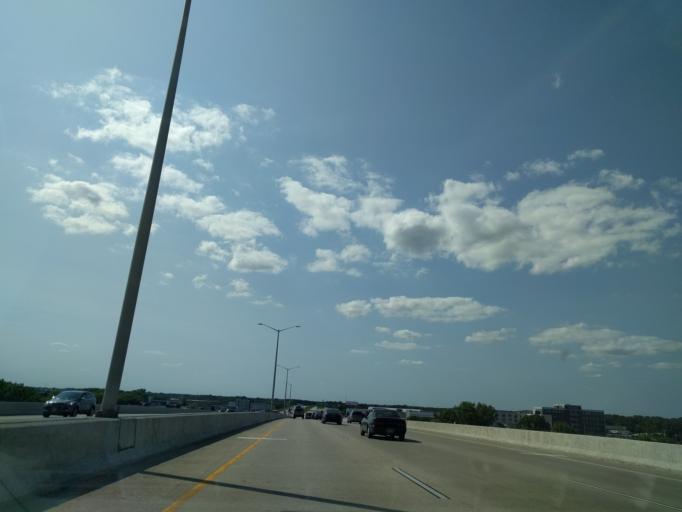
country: US
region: Wisconsin
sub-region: Brown County
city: Ashwaubenon
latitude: 44.4761
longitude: -88.0473
